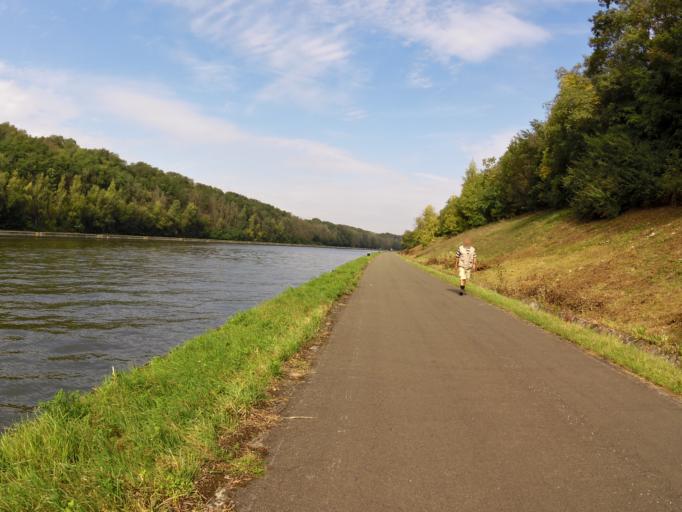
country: BE
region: Flanders
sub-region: Provincie Limburg
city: Riemst
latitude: 50.8387
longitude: 5.6392
